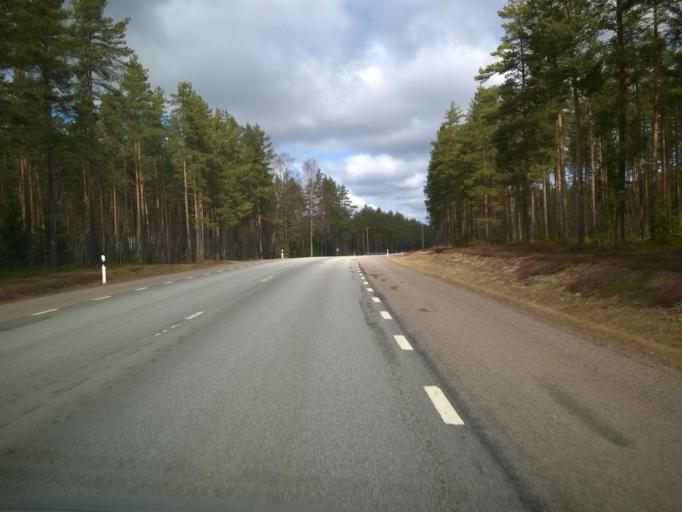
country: SE
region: Uppsala
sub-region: Tierps Kommun
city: Tierp
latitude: 60.1874
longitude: 17.4781
